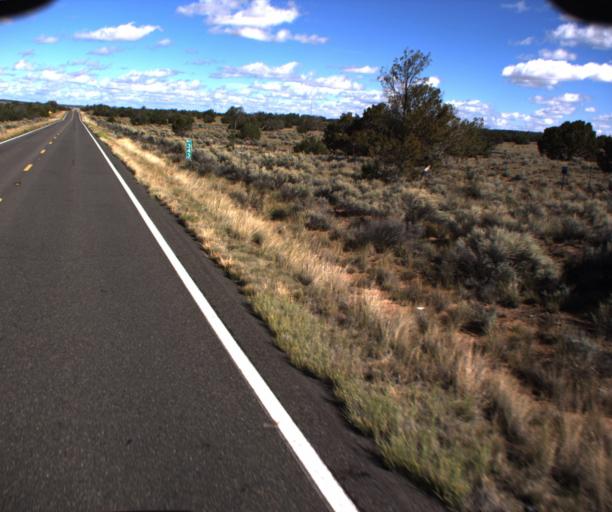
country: US
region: Arizona
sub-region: Apache County
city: Saint Johns
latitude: 34.8784
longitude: -109.2379
